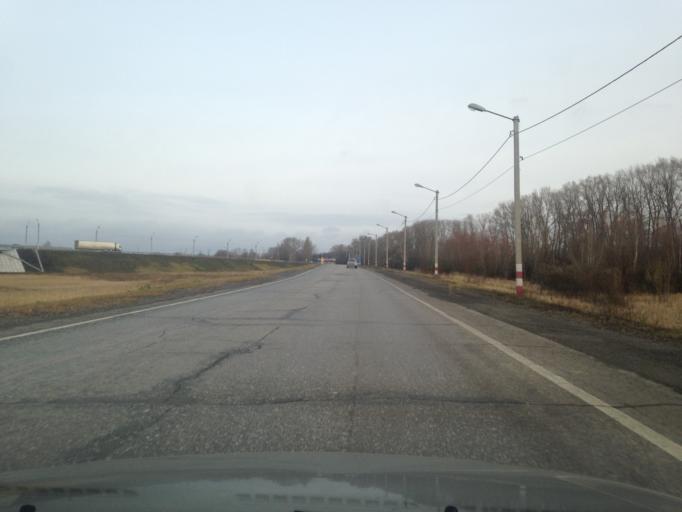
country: RU
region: Ulyanovsk
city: Novoul'yanovsk
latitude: 54.2090
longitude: 48.2959
